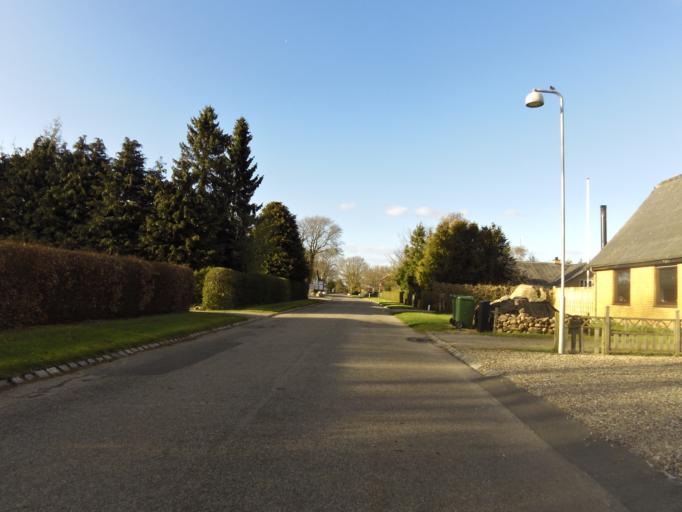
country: DK
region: South Denmark
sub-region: Tonder Kommune
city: Toftlund
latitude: 55.2327
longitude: 9.1242
